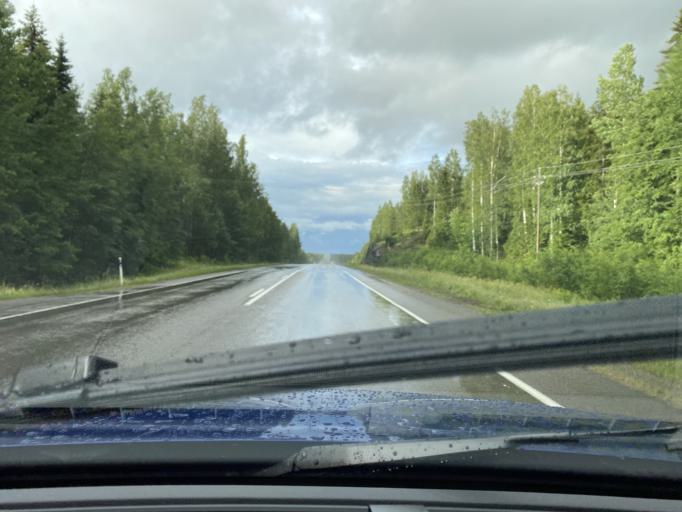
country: FI
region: Uusimaa
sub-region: Helsinki
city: Nurmijaervi
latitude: 60.4632
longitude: 24.8348
